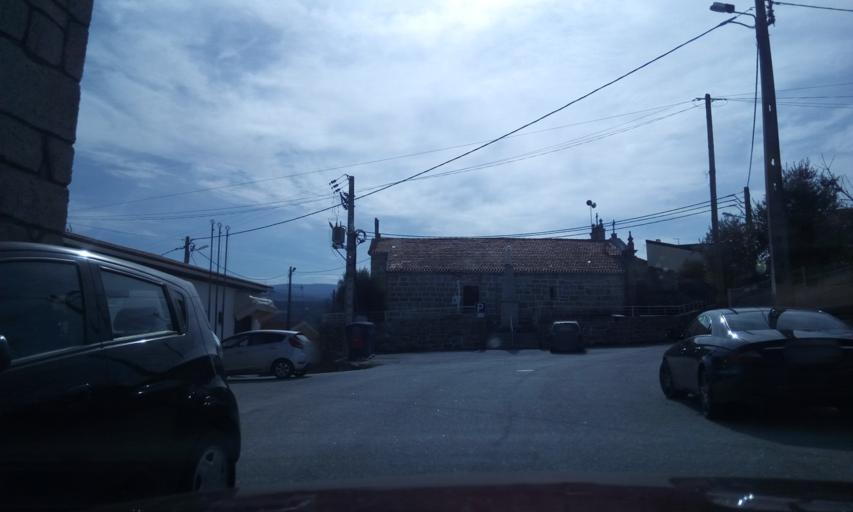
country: PT
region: Guarda
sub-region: Celorico da Beira
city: Celorico da Beira
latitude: 40.6277
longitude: -7.4368
